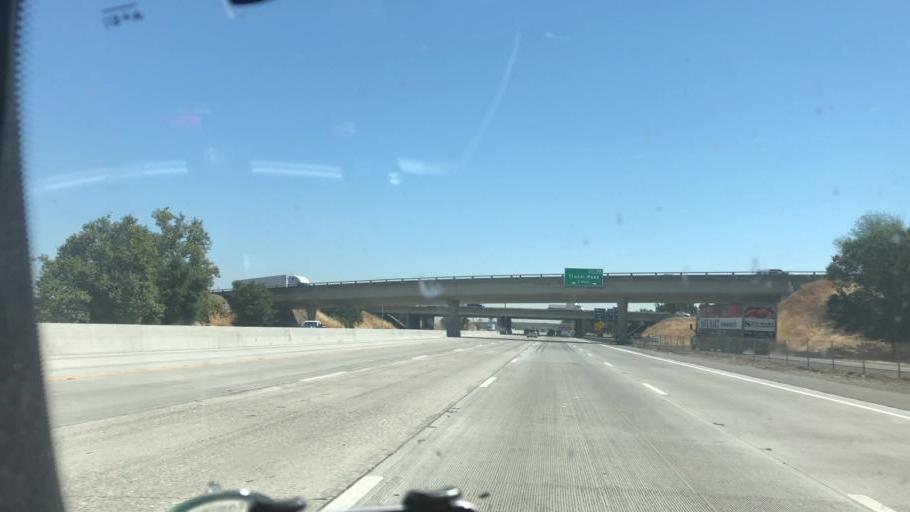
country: US
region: California
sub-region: Yolo County
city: West Sacramento
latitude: 38.6235
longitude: -121.5198
